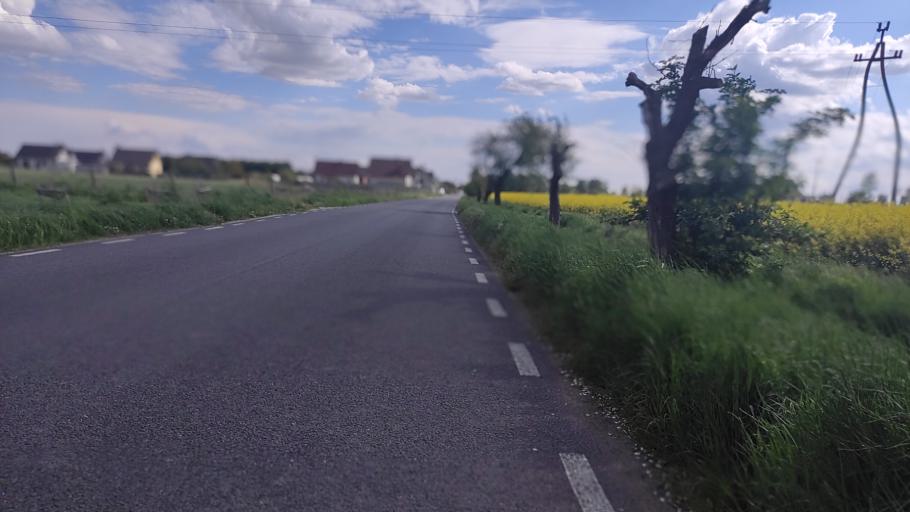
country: PL
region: Greater Poland Voivodeship
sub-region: Powiat poznanski
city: Kostrzyn
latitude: 52.4073
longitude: 17.1662
